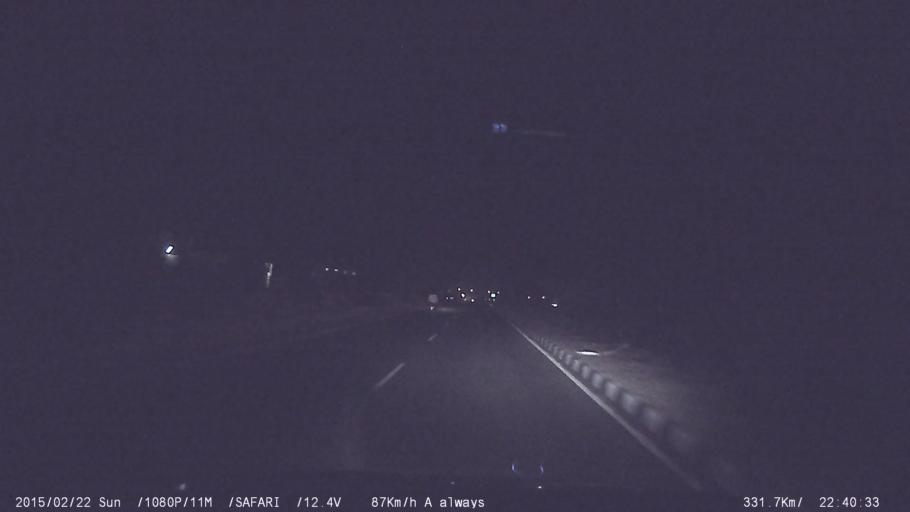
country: IN
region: Tamil Nadu
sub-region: Namakkal
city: Velur
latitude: 11.1777
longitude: 78.0595
